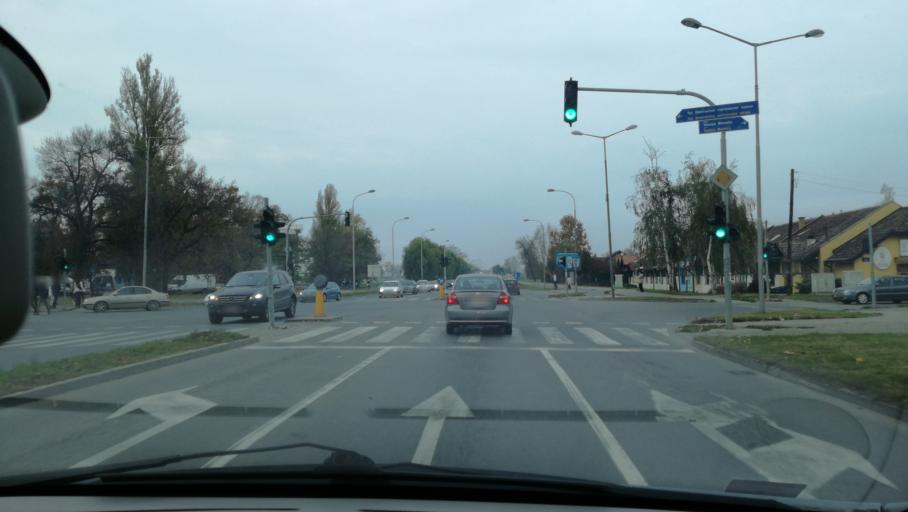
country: RS
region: Autonomna Pokrajina Vojvodina
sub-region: Juznobacki Okrug
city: Novi Sad
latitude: 45.2729
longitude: 19.8305
